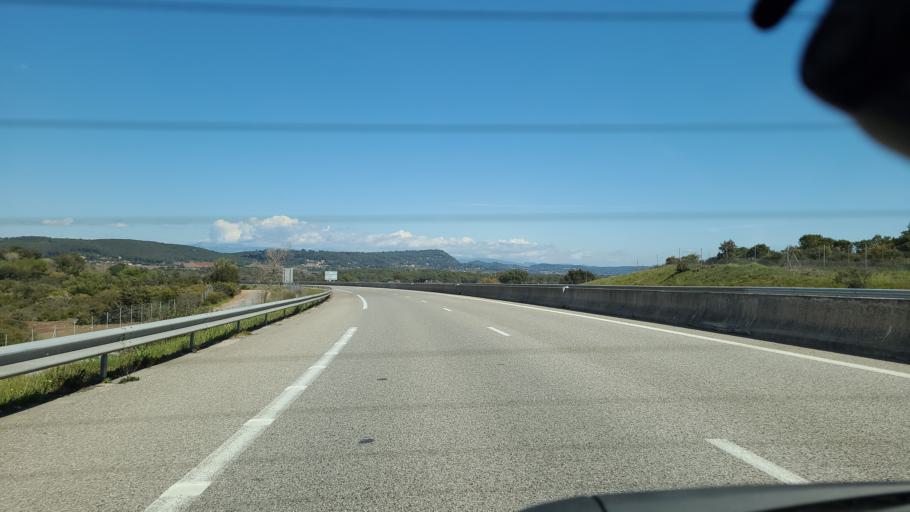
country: FR
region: Provence-Alpes-Cote d'Azur
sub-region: Departement du Var
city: Le Cannet-des-Maures
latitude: 43.3797
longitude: 6.3565
